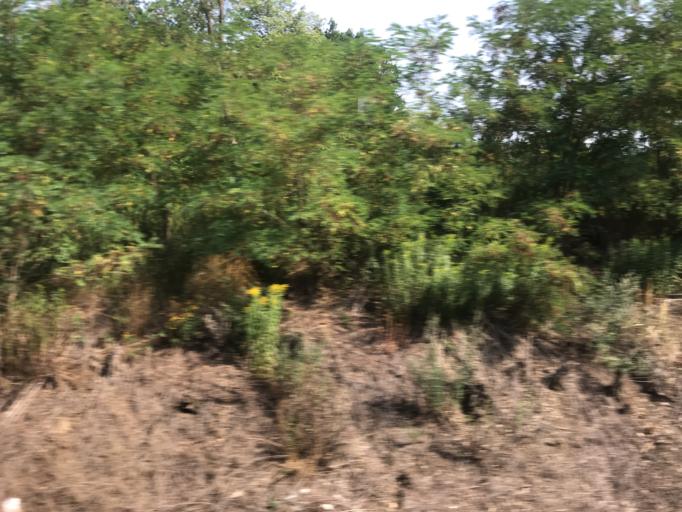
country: CZ
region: Central Bohemia
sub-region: Okres Benesov
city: Cercany
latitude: 49.8761
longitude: 14.7216
